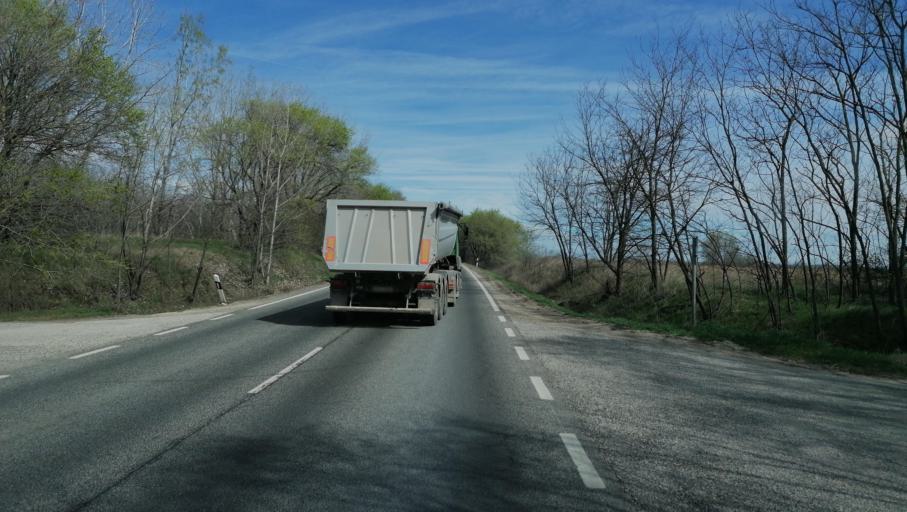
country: HU
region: Pest
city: Ocsa
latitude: 47.3097
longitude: 19.1965
